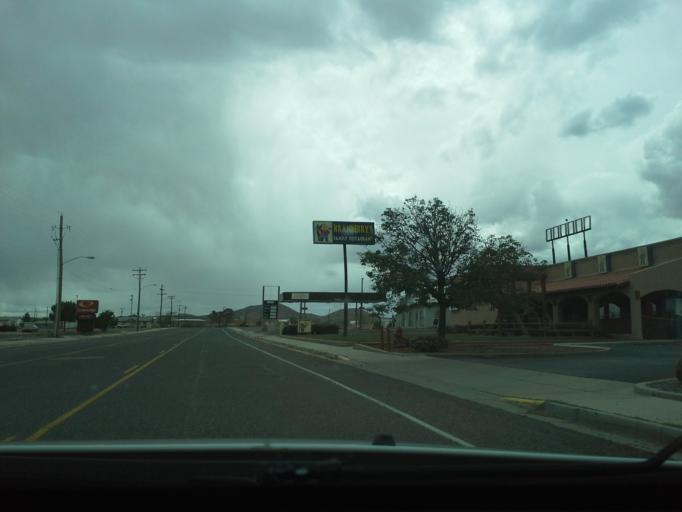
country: US
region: New Mexico
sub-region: Hidalgo County
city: Lordsburg
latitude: 32.3412
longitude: -108.7143
